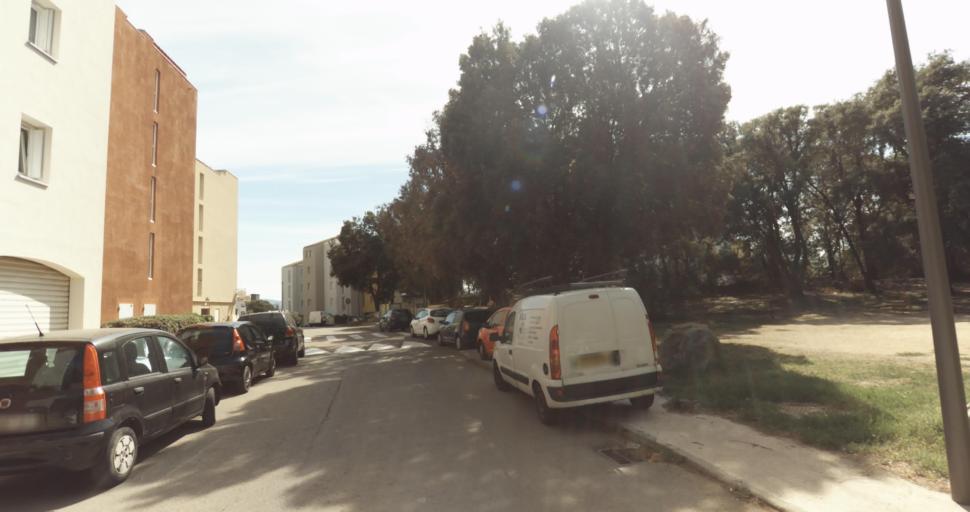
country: FR
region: Corsica
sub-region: Departement de la Corse-du-Sud
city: Ajaccio
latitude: 41.9483
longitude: 8.7533
